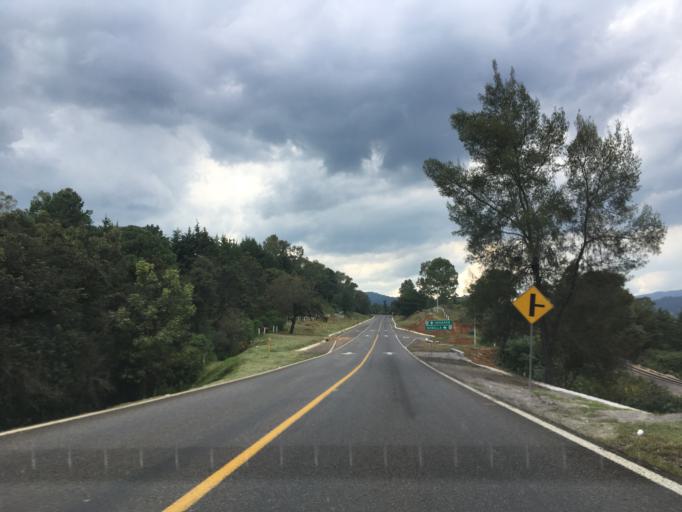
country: MX
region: Michoacan
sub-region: Patzcuaro
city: Santa Ana Chapitiro
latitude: 19.5077
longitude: -101.6963
